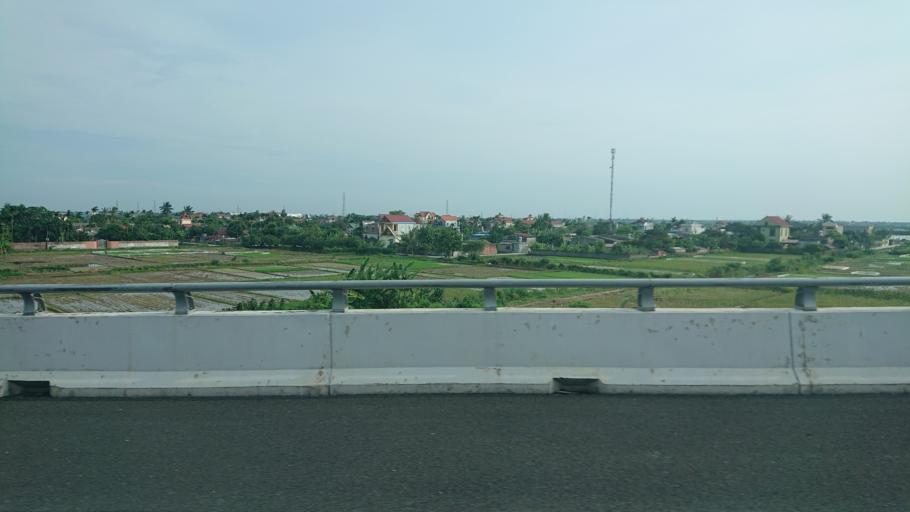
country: VN
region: Hai Phong
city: An Lao
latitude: 20.8063
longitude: 106.5170
